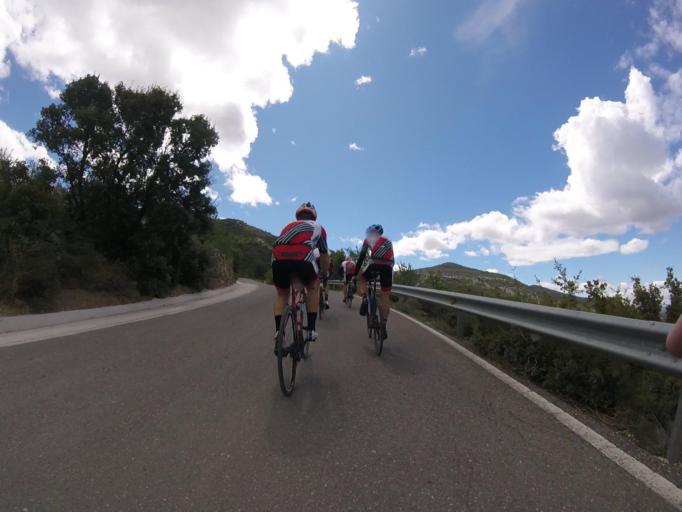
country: ES
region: Valencia
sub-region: Provincia de Castello
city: Sierra-Engarceran
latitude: 40.2938
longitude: -0.0414
